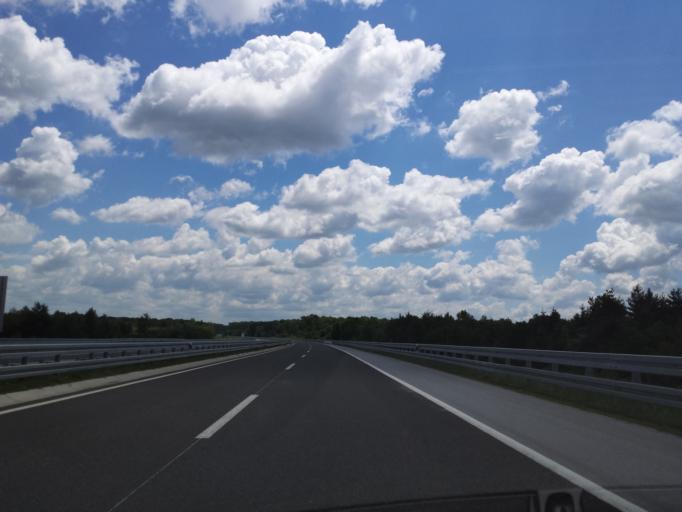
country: HR
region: Sisacko-Moslavacka
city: Lekenik
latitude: 45.5889
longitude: 16.1698
